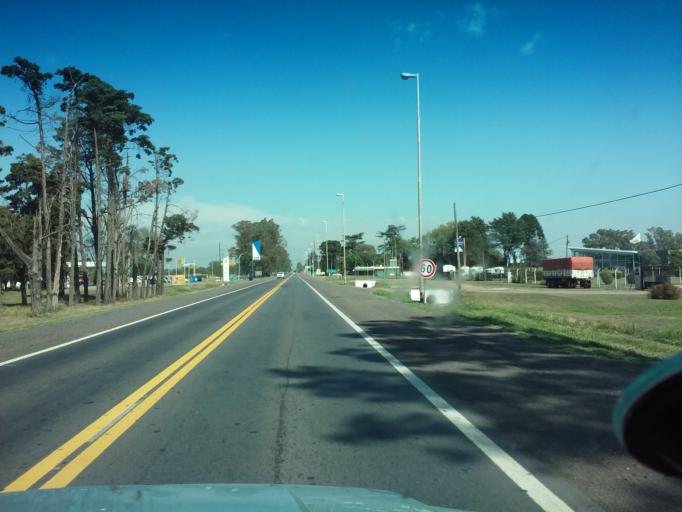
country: AR
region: Buenos Aires
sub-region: Partido de Nueve de Julio
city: Nueve de Julio
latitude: -35.4791
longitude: -60.8710
